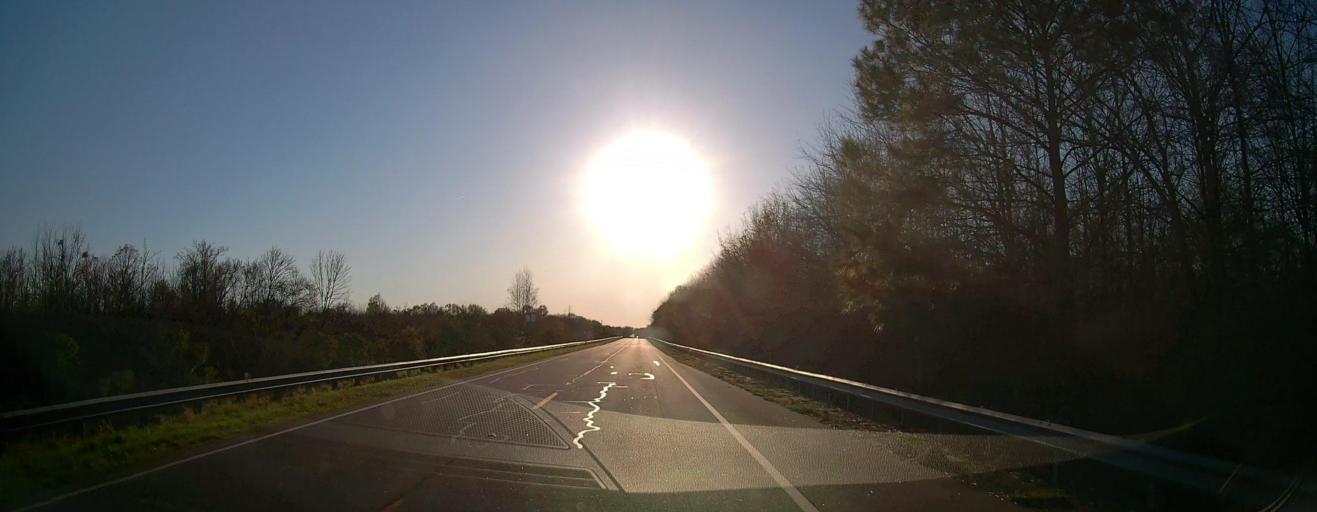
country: US
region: Georgia
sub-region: Wilcox County
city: Abbeville
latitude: 31.9977
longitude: -83.2736
